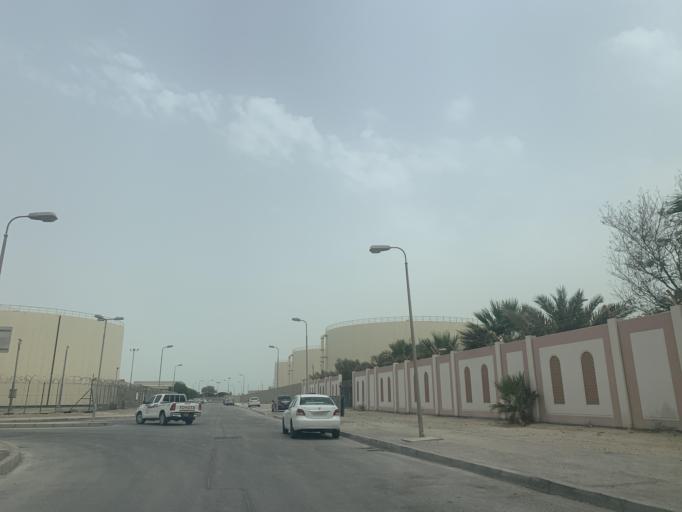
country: BH
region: Northern
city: Sitrah
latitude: 26.1797
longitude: 50.6189
